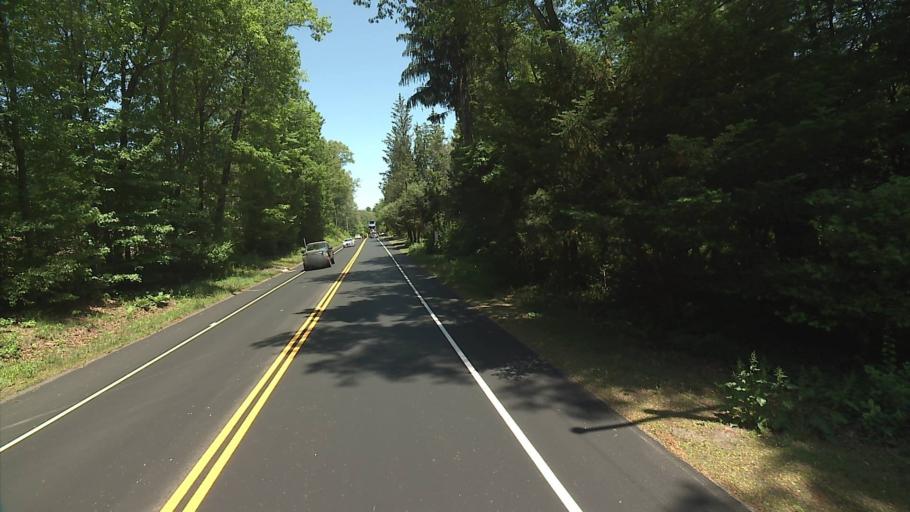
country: US
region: Connecticut
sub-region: Tolland County
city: Crystal Lake
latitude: 41.9350
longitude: -72.3814
